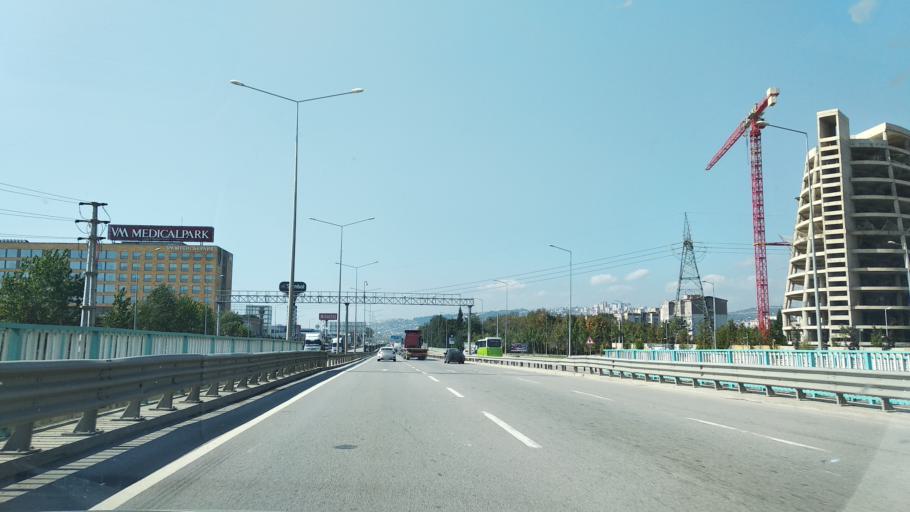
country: TR
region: Kocaeli
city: Kosekoy
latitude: 40.7591
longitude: 29.9838
